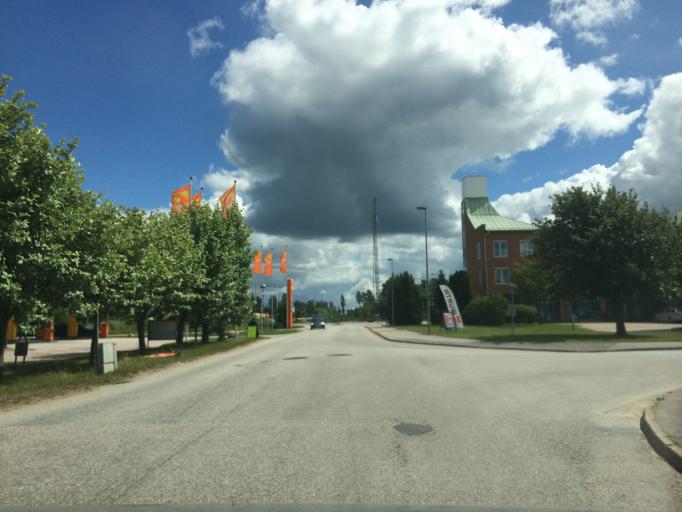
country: SE
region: Vaestra Goetaland
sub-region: Trollhattan
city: Trollhattan
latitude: 58.2987
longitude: 12.3204
